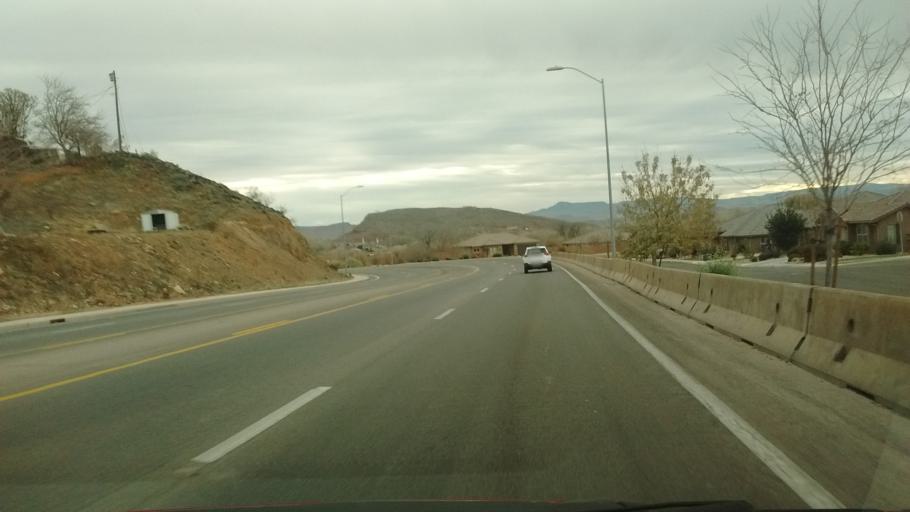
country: US
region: Utah
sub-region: Washington County
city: Washington
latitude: 37.1201
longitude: -113.5047
